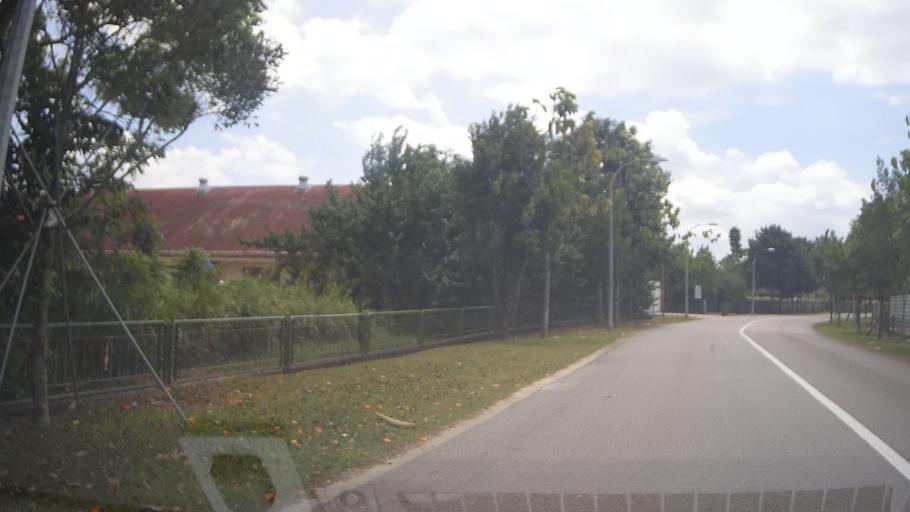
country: MY
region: Johor
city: Johor Bahru
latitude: 1.4441
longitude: 103.7313
